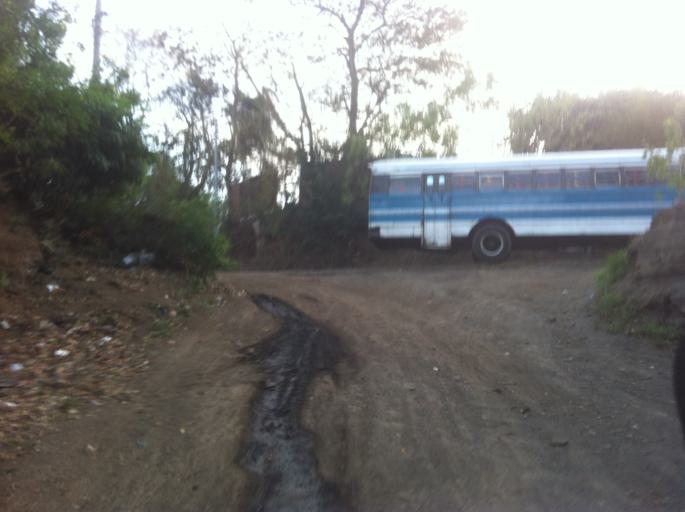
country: NI
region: Managua
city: Ciudad Sandino
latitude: 12.0950
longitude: -86.3342
